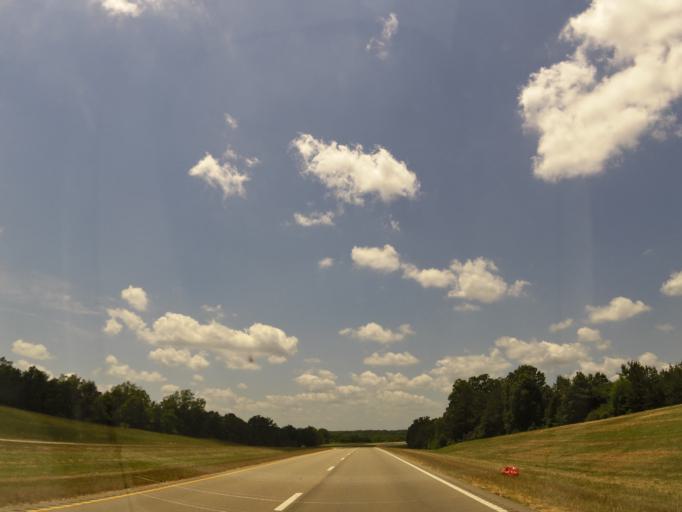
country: US
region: Mississippi
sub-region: Pontotoc County
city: Pontotoc
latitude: 34.2212
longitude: -88.8648
